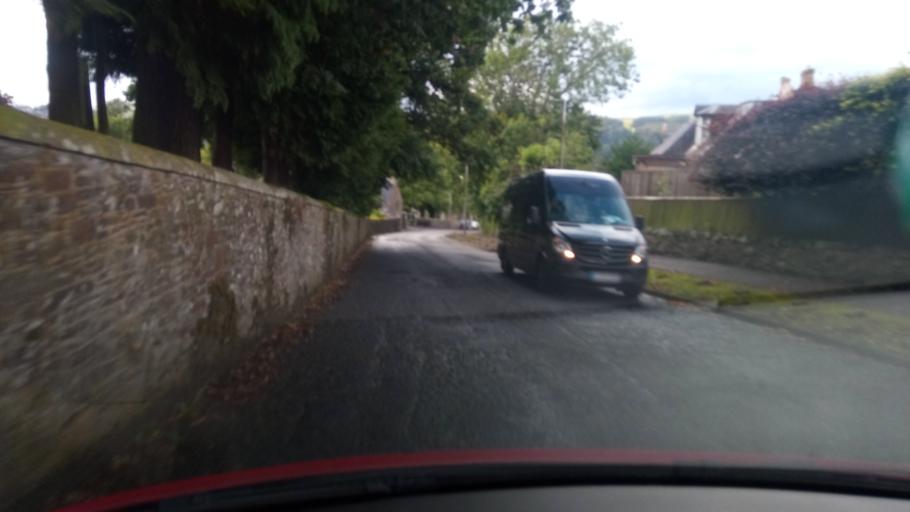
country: GB
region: Scotland
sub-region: The Scottish Borders
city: Hawick
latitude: 55.4202
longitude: -2.7824
